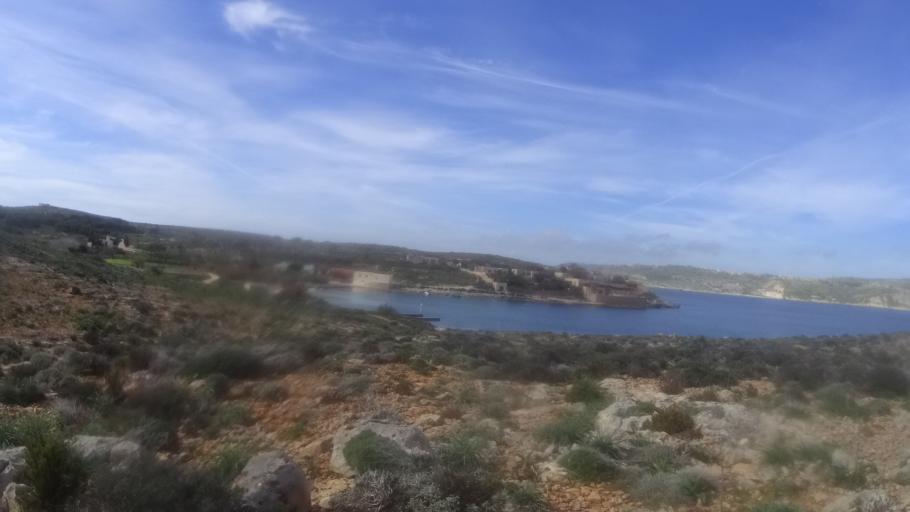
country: MT
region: Il-Qala
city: Qala
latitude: 36.0164
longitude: 14.3392
